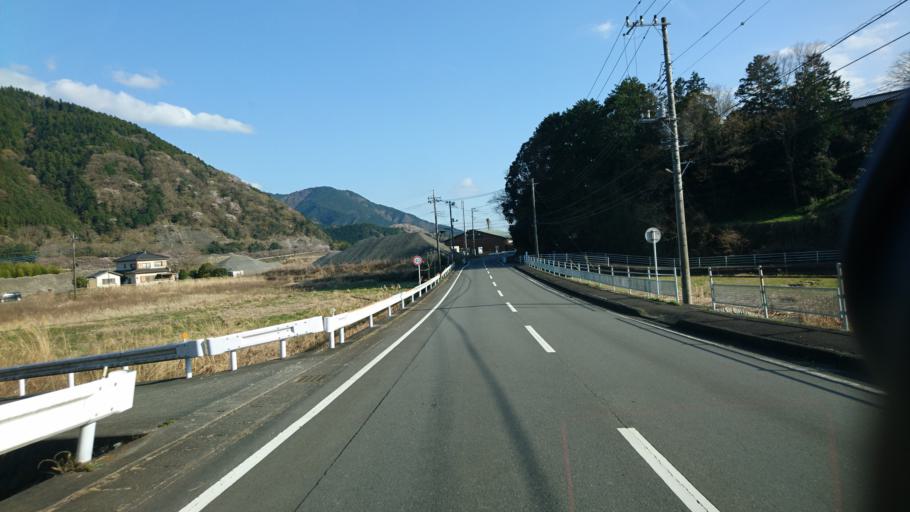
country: JP
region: Shizuoka
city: Fujinomiya
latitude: 35.3008
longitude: 138.4502
